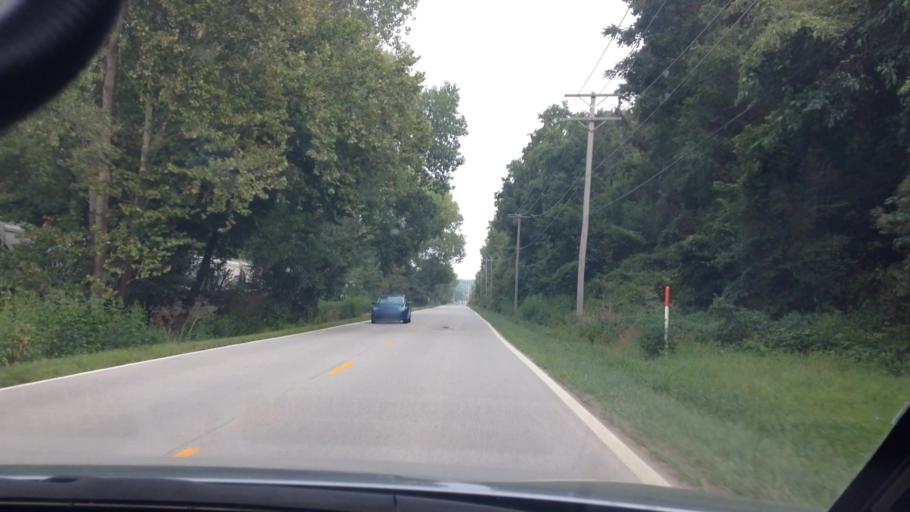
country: US
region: Kansas
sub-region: Leavenworth County
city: Lansing
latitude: 39.1969
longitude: -94.8121
